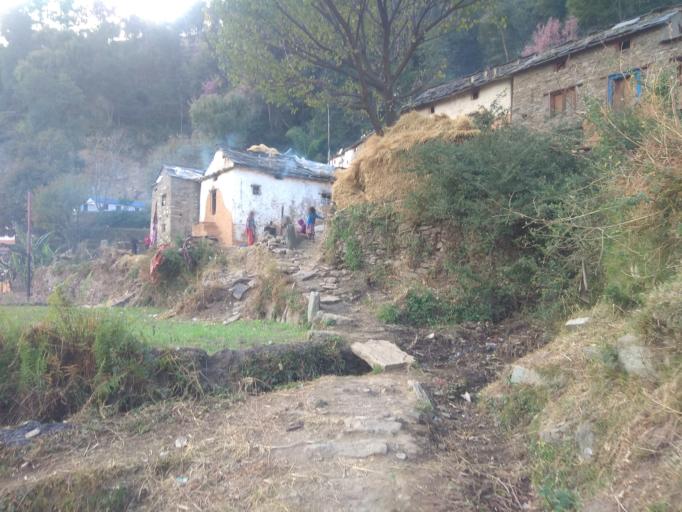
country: NP
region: Mid Western
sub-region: Bheri Zone
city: Dailekh
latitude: 29.2519
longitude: 81.6611
